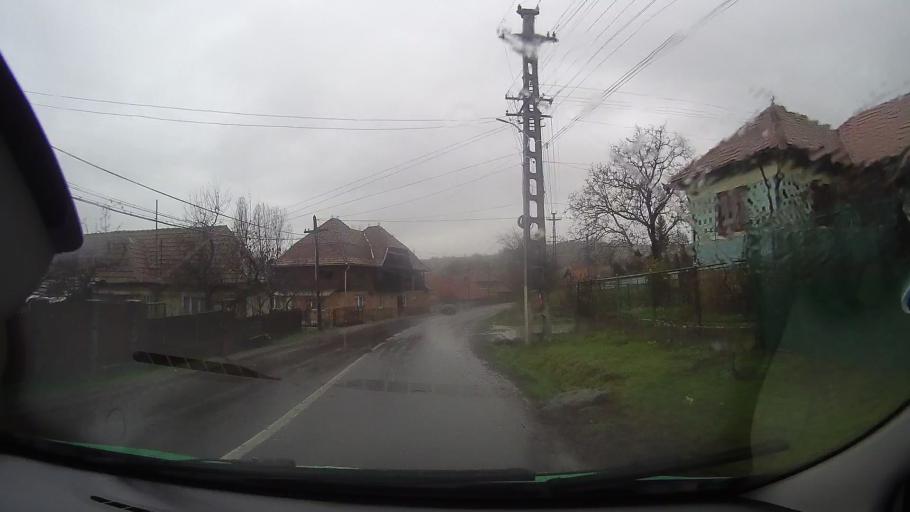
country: RO
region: Mures
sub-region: Comuna Vatava
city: Vatava
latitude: 46.9592
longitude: 24.7628
